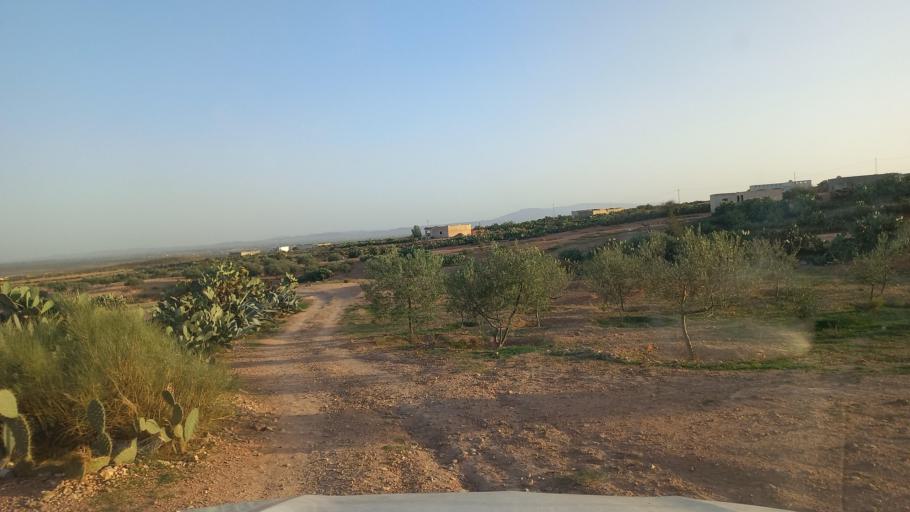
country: TN
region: Al Qasrayn
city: Sbiba
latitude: 35.3736
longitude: 9.0046
